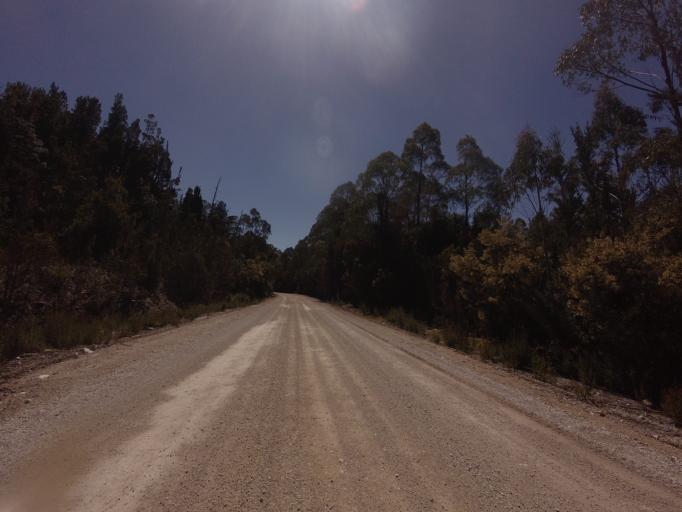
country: AU
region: Tasmania
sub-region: Huon Valley
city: Geeveston
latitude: -42.8237
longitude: 146.3897
